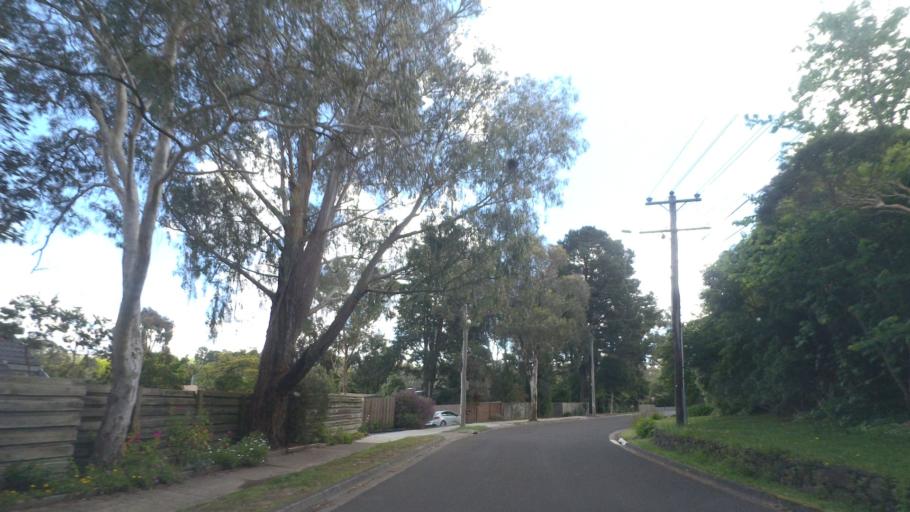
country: AU
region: Victoria
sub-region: Maroondah
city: Croydon South
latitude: -37.8105
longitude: 145.2627
